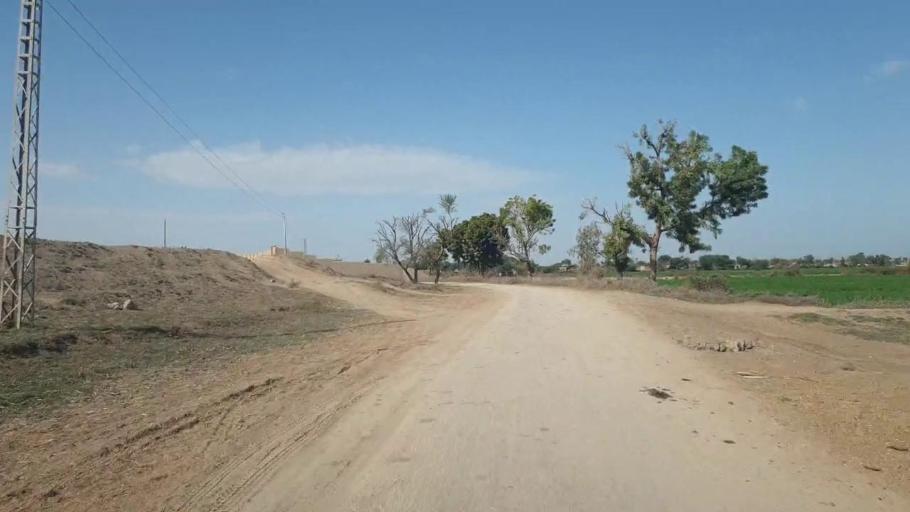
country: PK
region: Sindh
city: Sakrand
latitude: 25.9718
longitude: 68.3374
